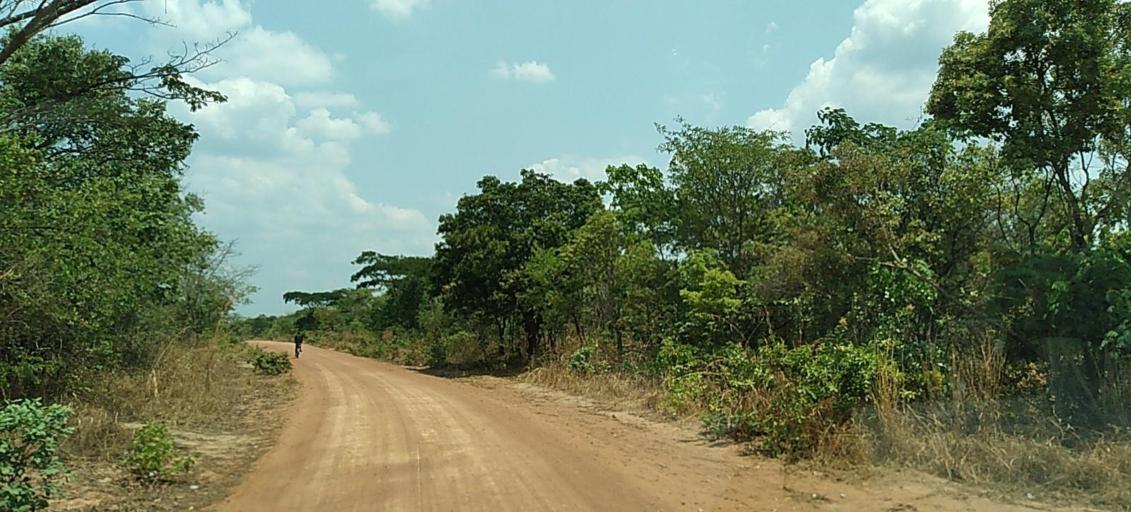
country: ZM
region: Copperbelt
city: Luanshya
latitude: -13.1395
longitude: 28.3145
